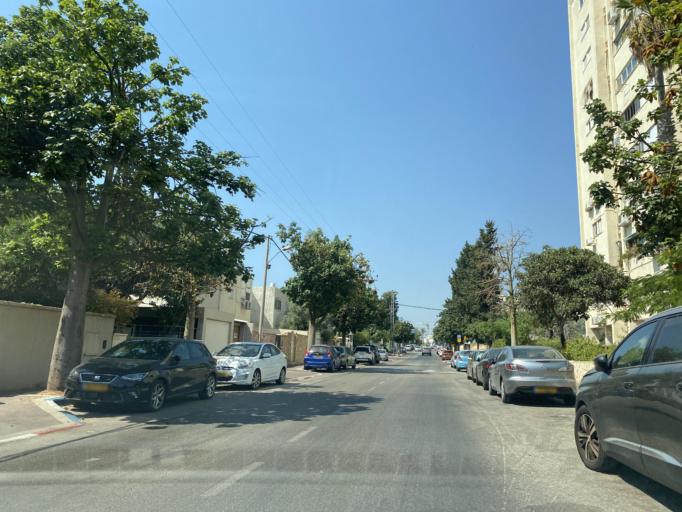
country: IL
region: Tel Aviv
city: Ramat HaSharon
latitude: 32.1344
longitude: 34.8377
